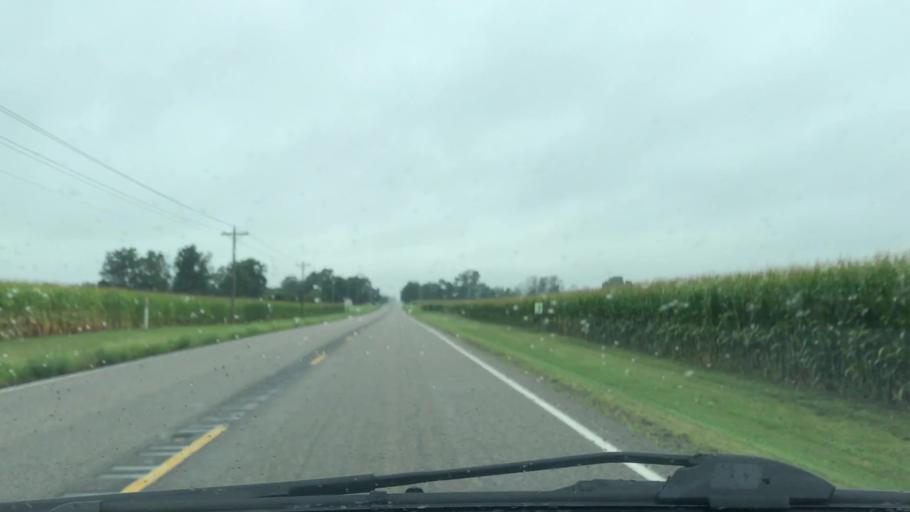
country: US
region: Indiana
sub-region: Boone County
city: Dale
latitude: 40.1270
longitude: -86.3676
